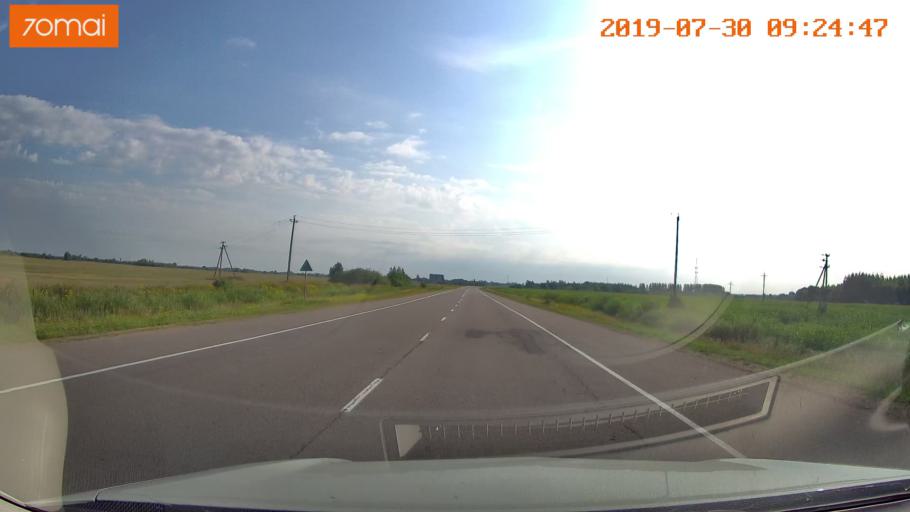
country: LT
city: Kybartai
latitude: 54.6346
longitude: 22.7020
